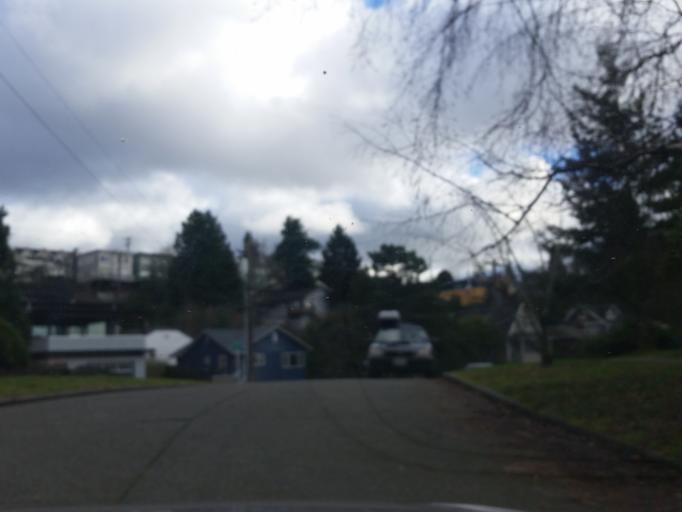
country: US
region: Washington
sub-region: King County
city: Seattle
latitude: 47.6601
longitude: -122.3577
